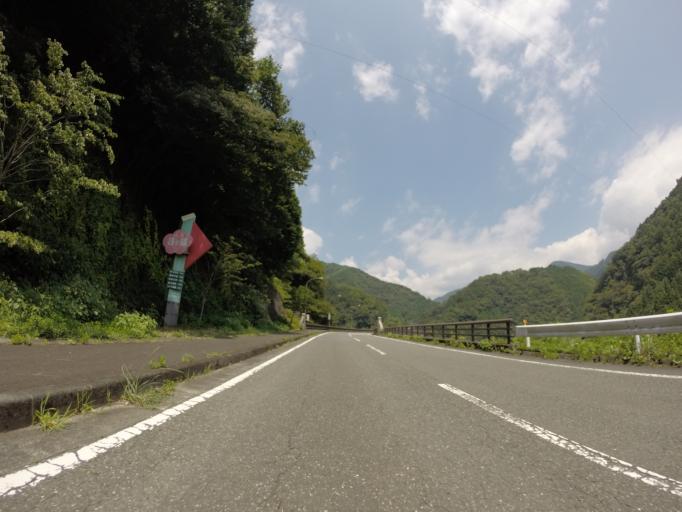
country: JP
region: Shizuoka
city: Shizuoka-shi
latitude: 35.2333
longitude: 138.3434
